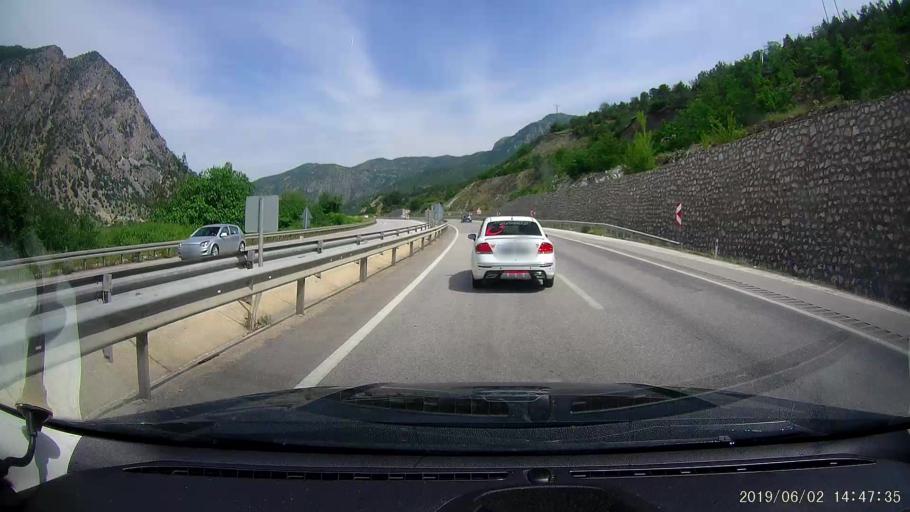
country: TR
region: Corum
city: Hacihamza
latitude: 41.0668
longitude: 34.4628
